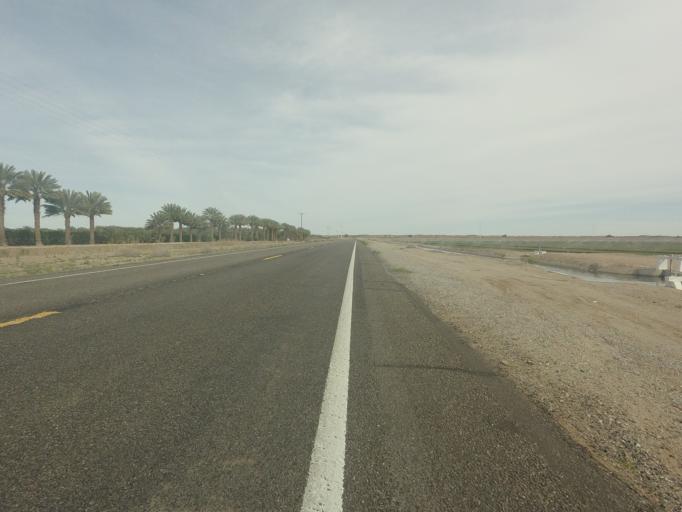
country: US
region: California
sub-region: Imperial County
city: Holtville
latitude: 32.9747
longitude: -115.3111
